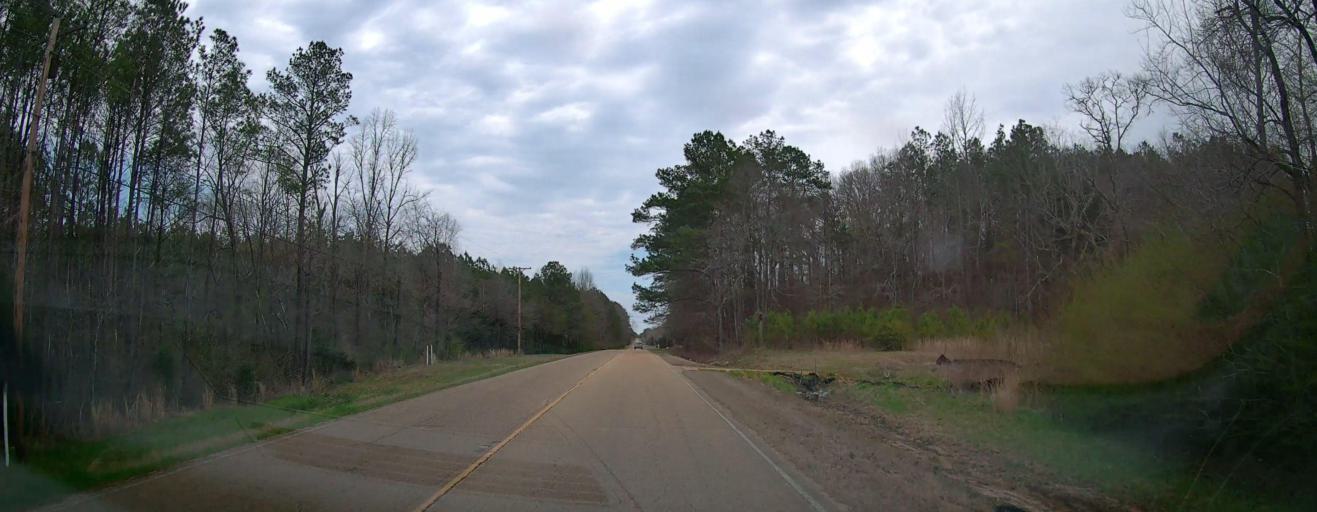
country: US
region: Mississippi
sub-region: Itawamba County
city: Fulton
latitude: 34.2288
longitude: -88.2377
